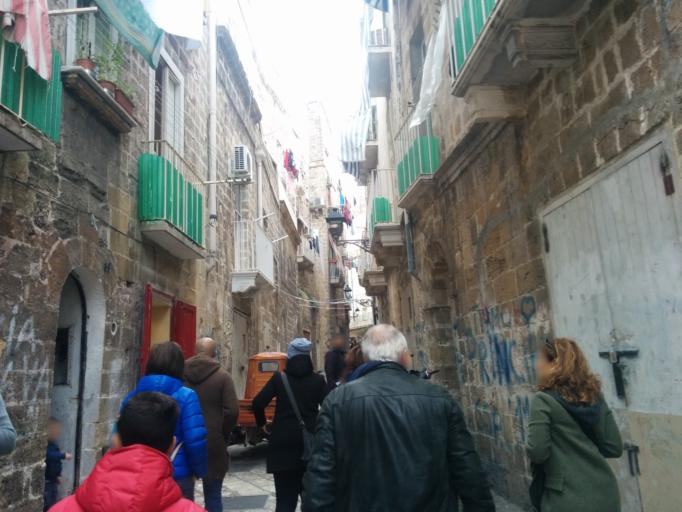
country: IT
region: Apulia
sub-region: Provincia di Taranto
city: Statte
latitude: 40.4775
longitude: 17.2284
